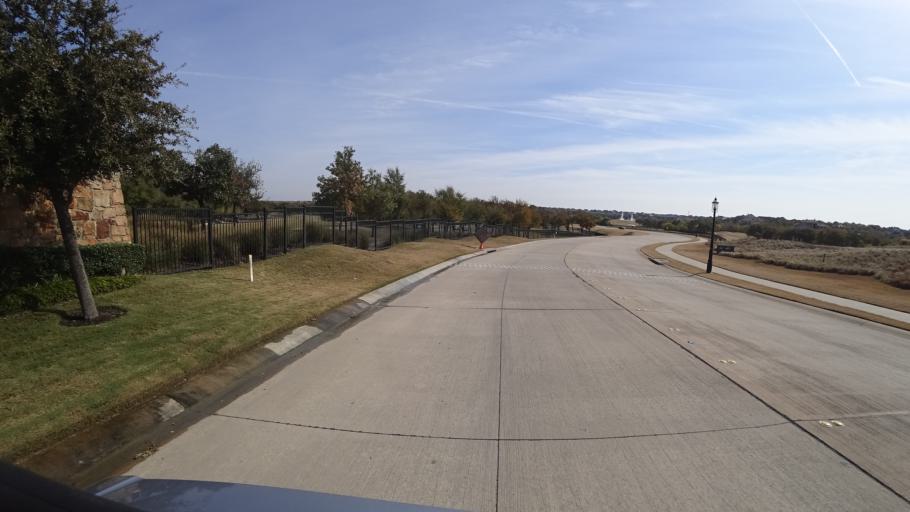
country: US
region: Texas
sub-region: Denton County
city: The Colony
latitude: 33.0424
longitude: -96.9047
